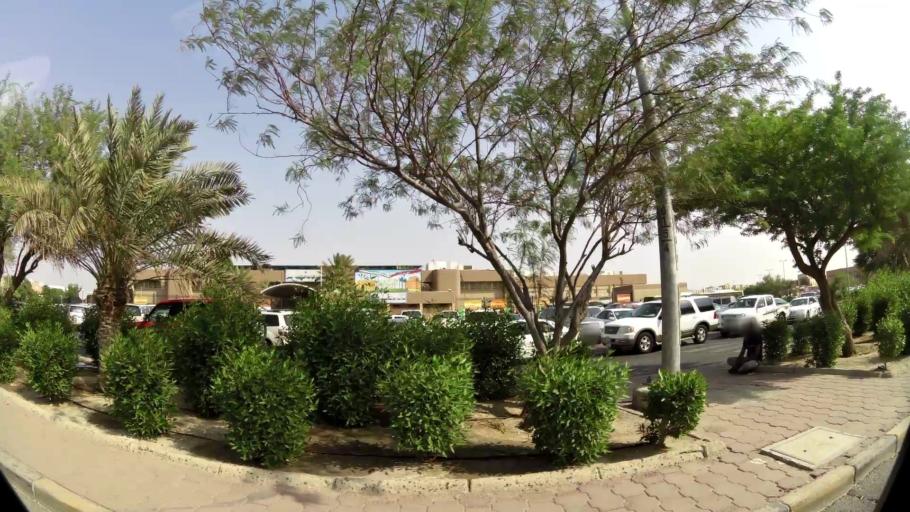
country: KW
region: Muhafazat al Jahra'
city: Al Jahra'
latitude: 29.3435
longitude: 47.6550
